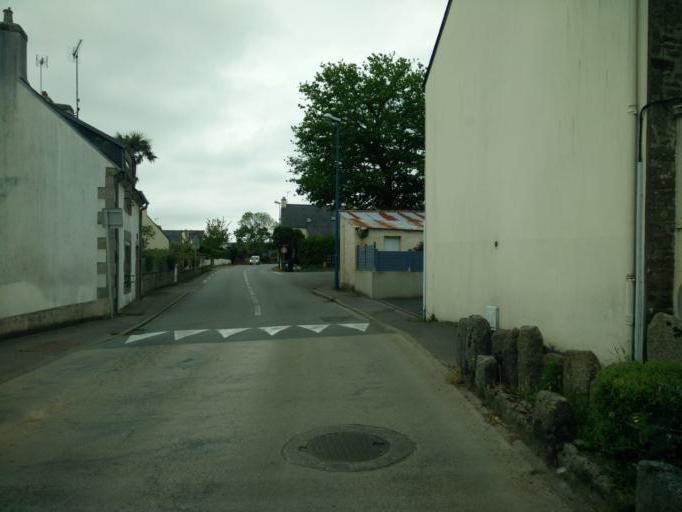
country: FR
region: Brittany
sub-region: Departement du Finistere
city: Tregunc
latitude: 47.8511
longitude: -3.8508
